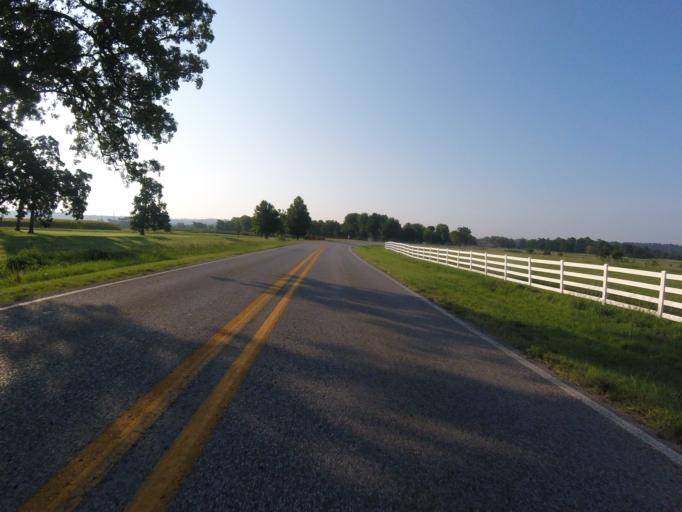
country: US
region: Arkansas
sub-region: Washington County
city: Fayetteville
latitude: 36.0937
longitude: -94.1758
